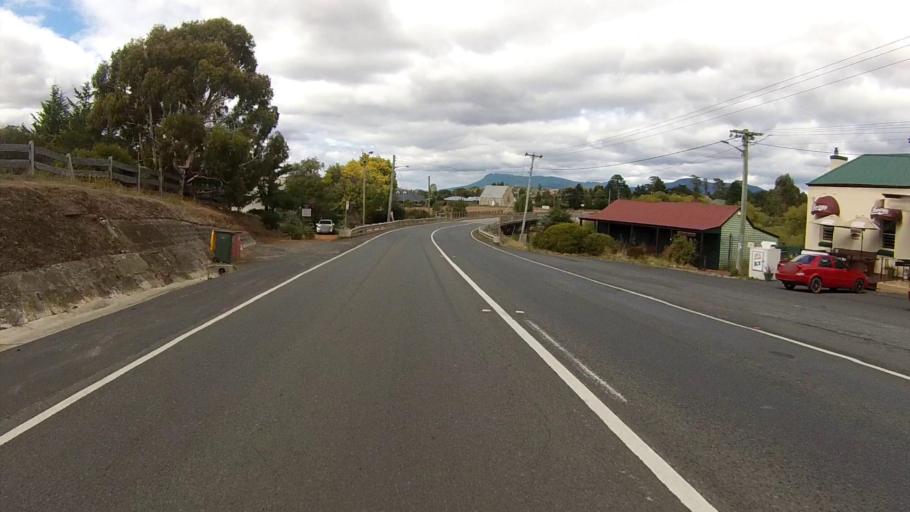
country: AU
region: Tasmania
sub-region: Brighton
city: Bridgewater
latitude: -42.6842
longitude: 147.2658
